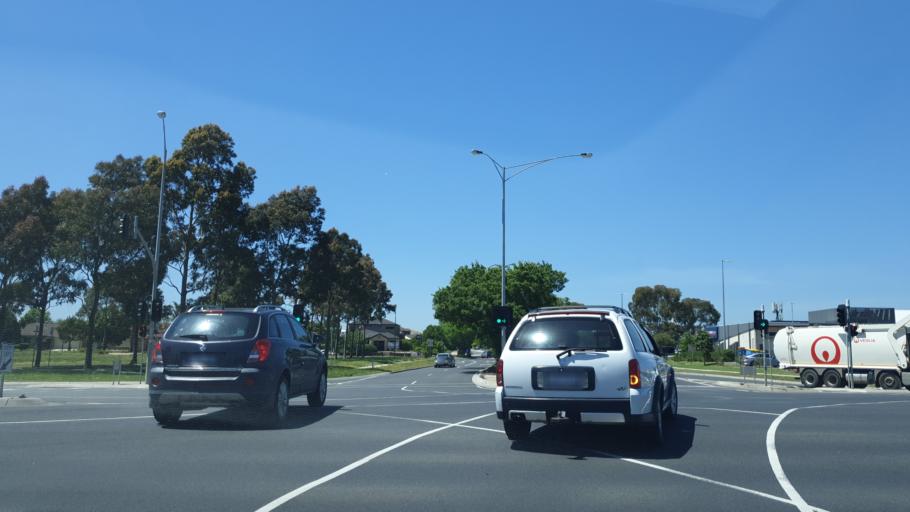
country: AU
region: Victoria
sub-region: Casey
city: Narre Warren South
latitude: -38.0652
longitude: 145.2988
